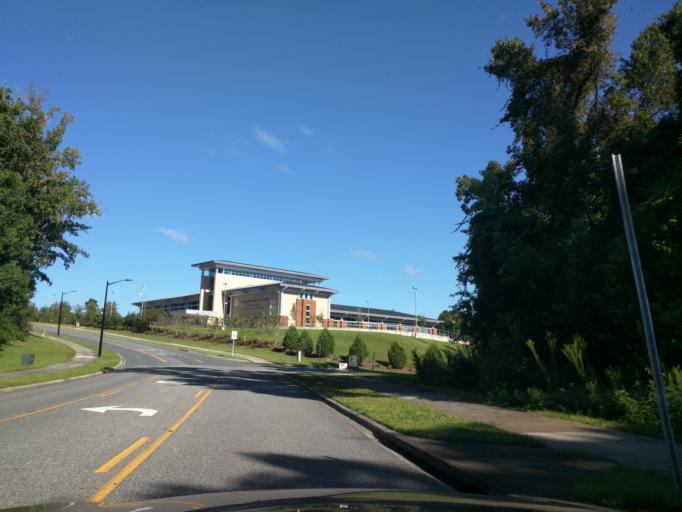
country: US
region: Florida
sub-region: Leon County
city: Tallahassee
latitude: 30.4594
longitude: -84.2548
